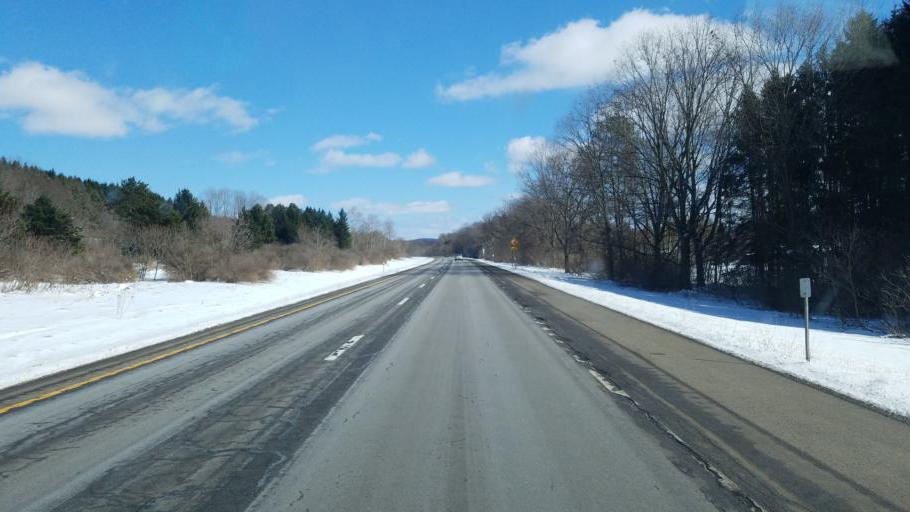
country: US
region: New York
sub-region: Chautauqua County
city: Falconer
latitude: 42.1350
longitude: -79.1491
